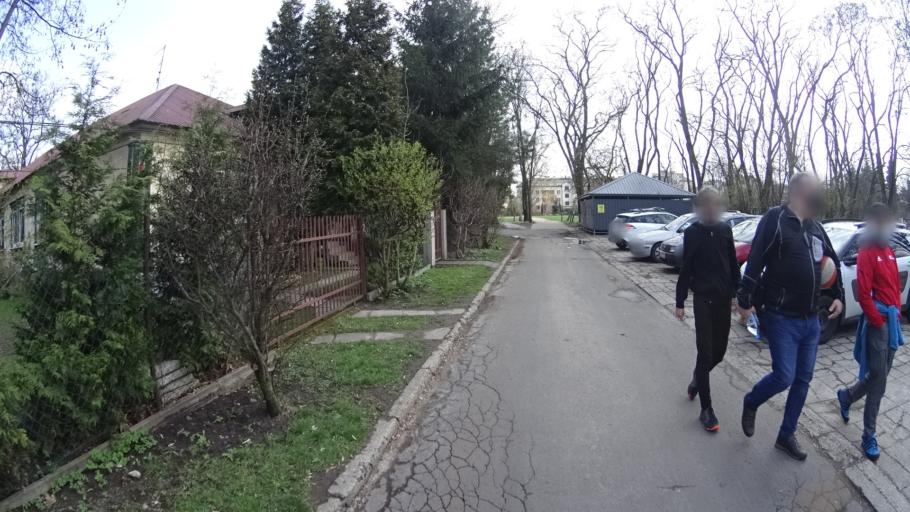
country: PL
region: Masovian Voivodeship
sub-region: Warszawa
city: Bemowo
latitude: 52.2367
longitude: 20.9199
